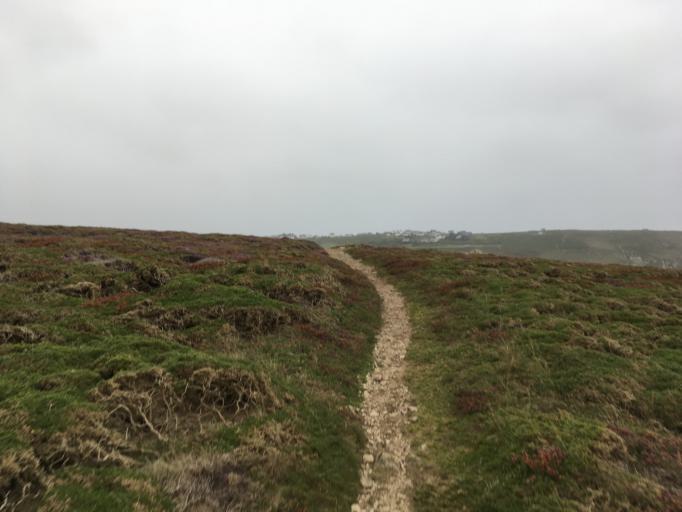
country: FR
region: Brittany
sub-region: Departement du Finistere
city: Plogoff
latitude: 48.0516
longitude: -4.7083
